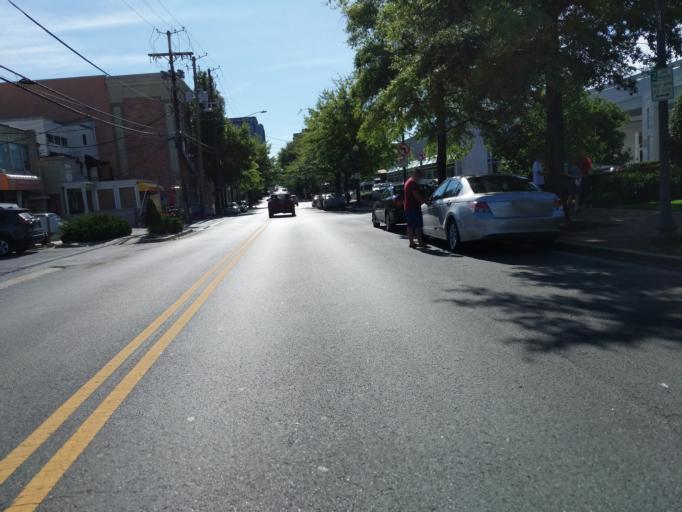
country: US
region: Maryland
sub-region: Montgomery County
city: Bethesda
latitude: 38.9808
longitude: -77.0998
